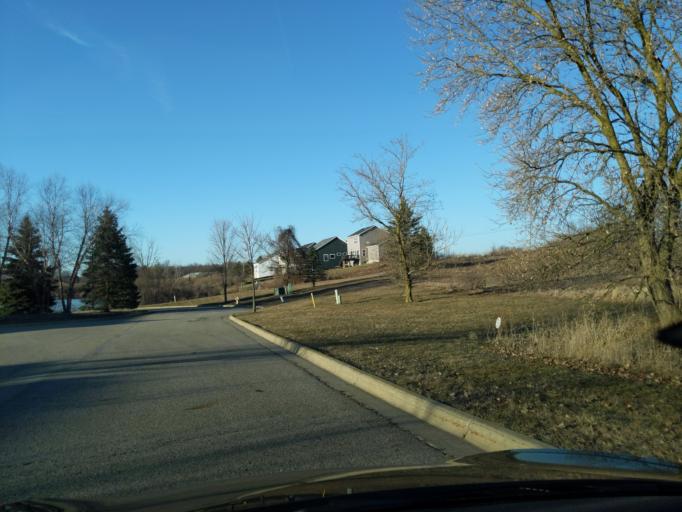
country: US
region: Michigan
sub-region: Ingham County
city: Mason
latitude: 42.5941
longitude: -84.4440
